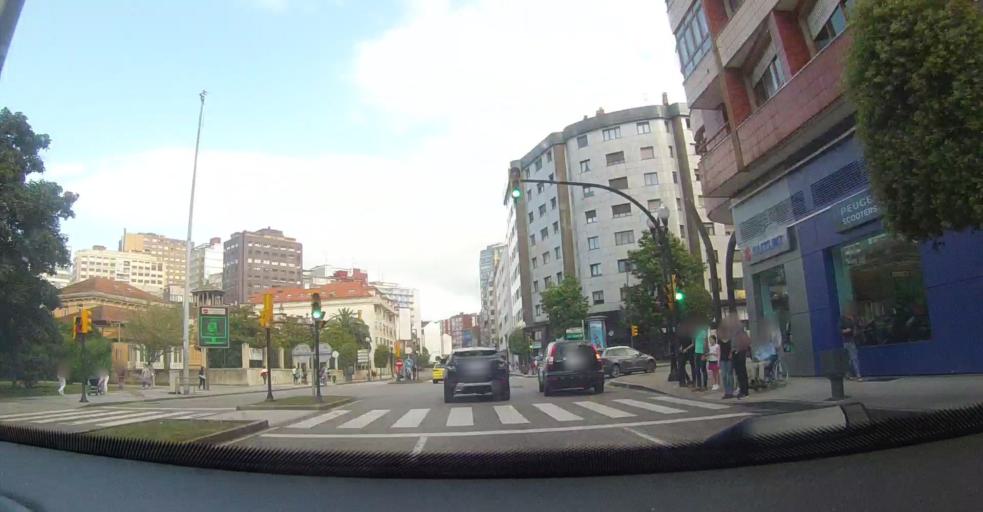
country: ES
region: Asturias
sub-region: Province of Asturias
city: Gijon
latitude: 43.5380
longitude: -5.6650
